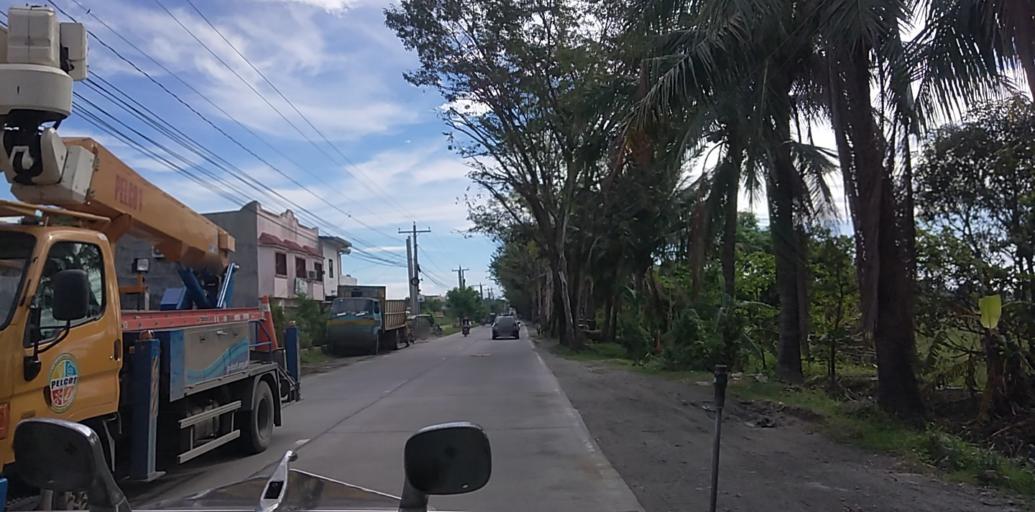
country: PH
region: Central Luzon
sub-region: Province of Pampanga
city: Arayat
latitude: 15.1497
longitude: 120.7539
